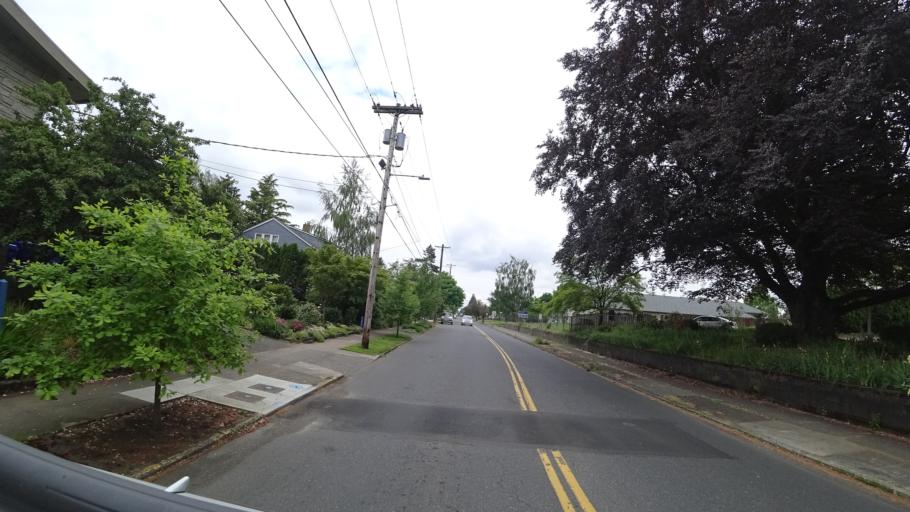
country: US
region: Oregon
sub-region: Multnomah County
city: Portland
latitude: 45.5195
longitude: -122.6151
